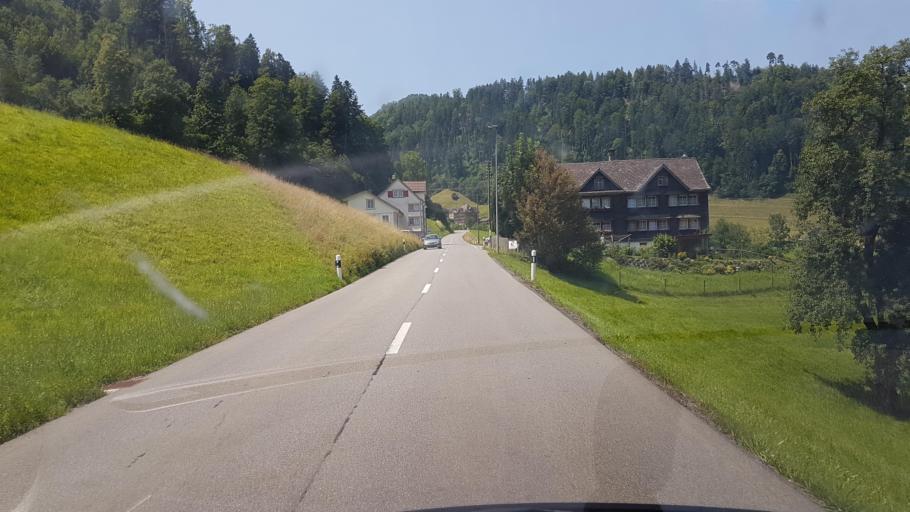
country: CH
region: Saint Gallen
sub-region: Wahlkreis Toggenburg
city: Mogelsberg
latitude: 47.3291
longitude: 9.1358
